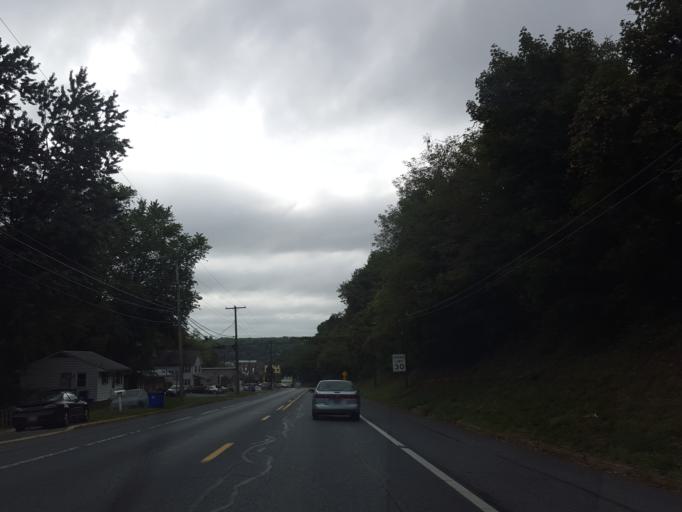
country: US
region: Maryland
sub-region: Frederick County
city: Brunswick
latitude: 39.3177
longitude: -77.6281
